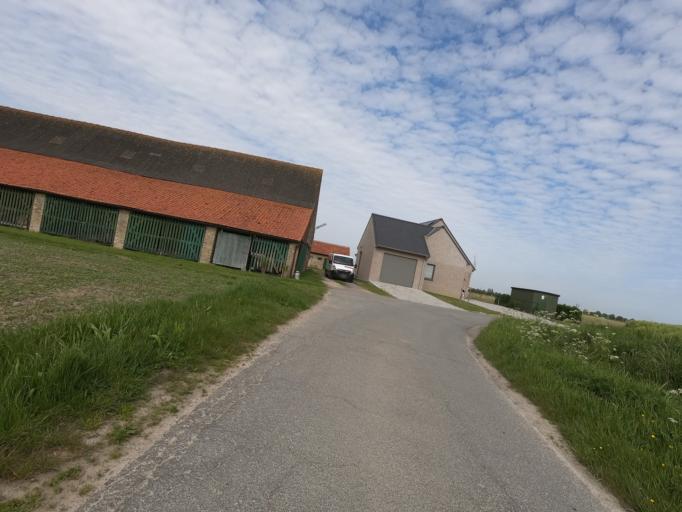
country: BE
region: Flanders
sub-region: Provincie West-Vlaanderen
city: Alveringem
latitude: 50.9683
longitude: 2.7169
